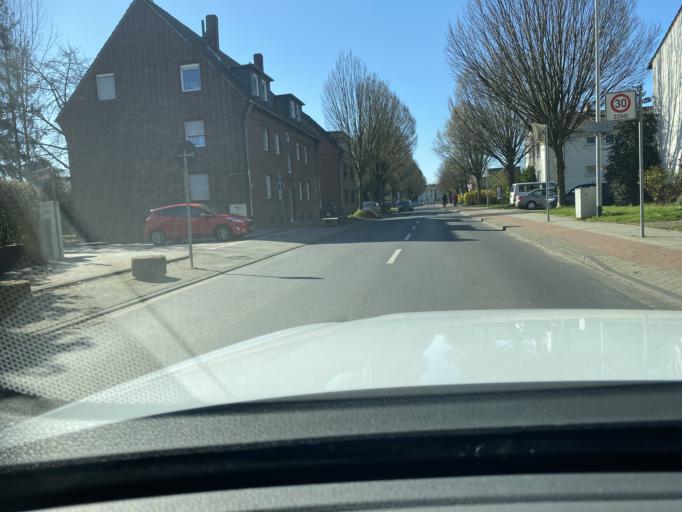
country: DE
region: North Rhine-Westphalia
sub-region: Regierungsbezirk Dusseldorf
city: Grevenbroich
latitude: 51.0954
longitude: 6.5822
